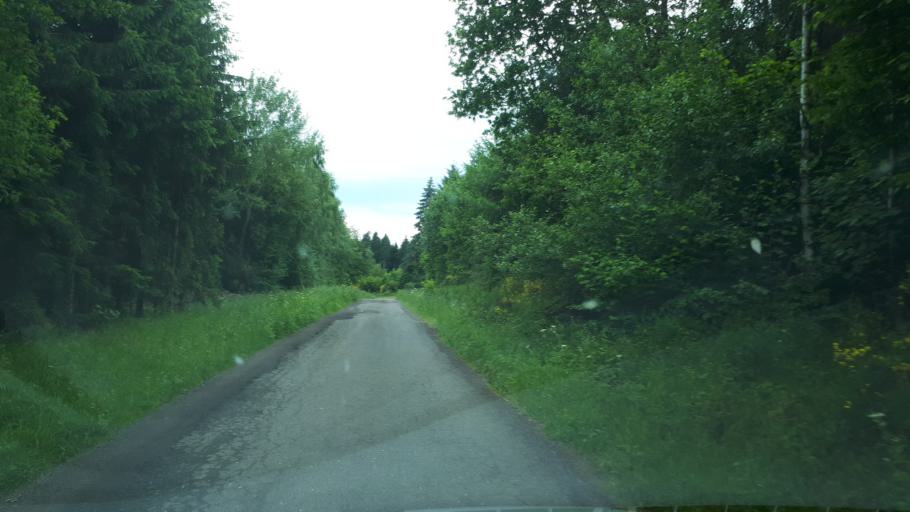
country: DE
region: Rheinland-Pfalz
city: Greimersburg
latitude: 50.2087
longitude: 7.1181
